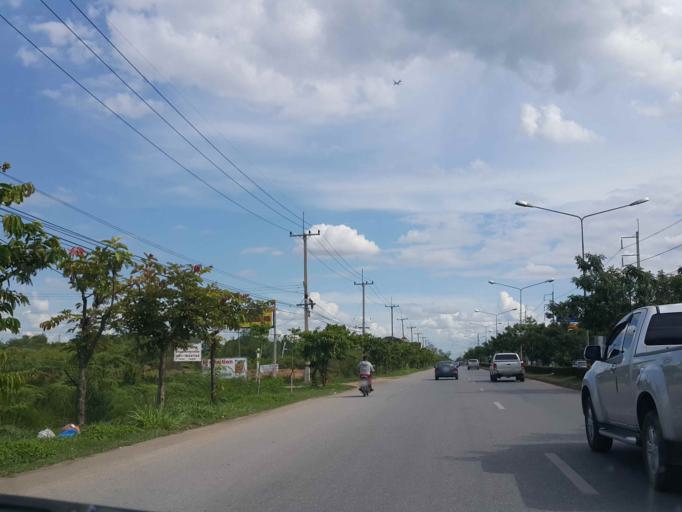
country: TH
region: Chiang Mai
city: San Sai
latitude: 18.8690
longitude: 99.0154
